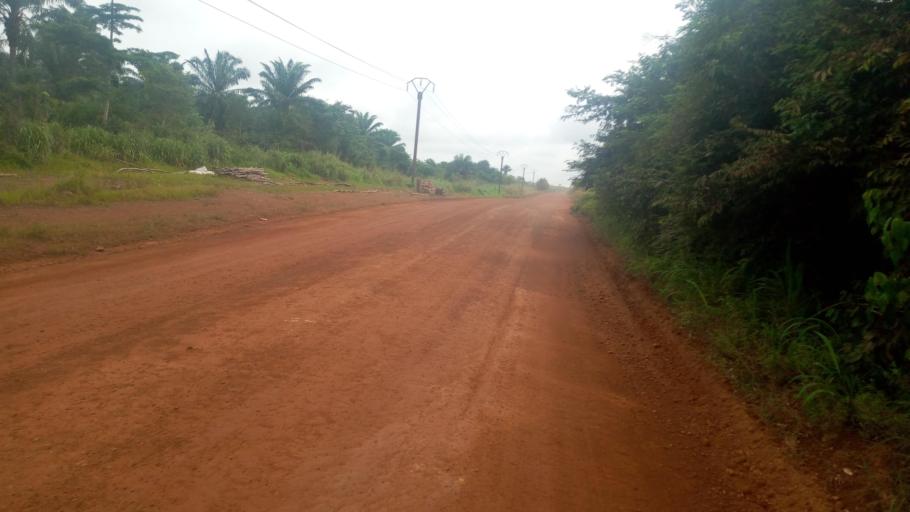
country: SL
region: Southern Province
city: Mogbwemo
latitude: 7.7145
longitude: -12.2852
